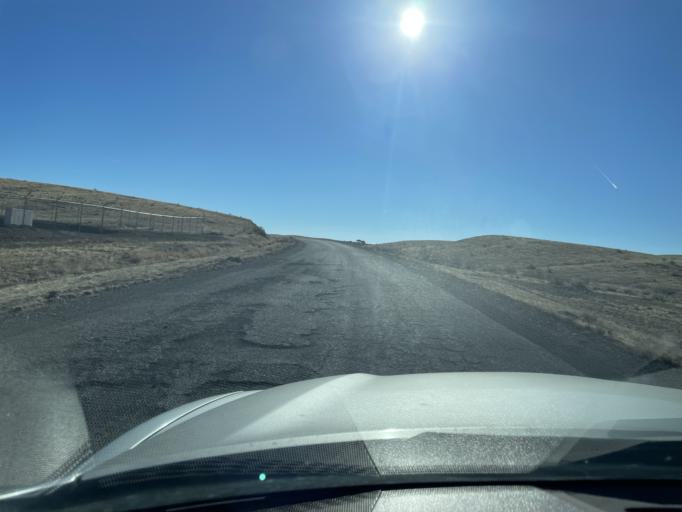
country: US
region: Colorado
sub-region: Mesa County
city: Loma
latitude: 39.2021
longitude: -109.1186
